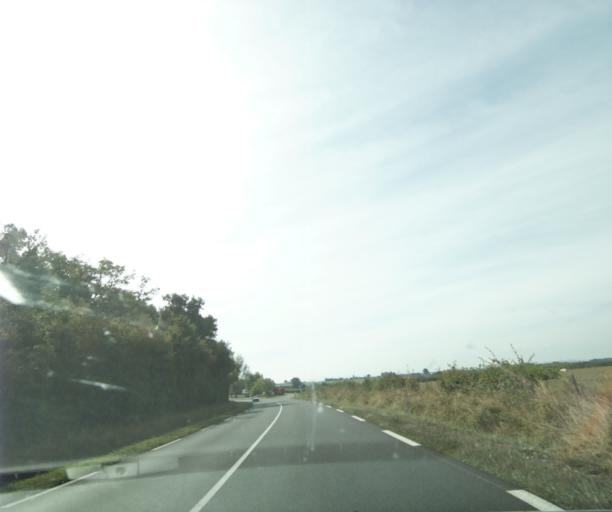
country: FR
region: Auvergne
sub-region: Departement de l'Allier
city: Saint-Francois
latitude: 46.4360
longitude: 3.9073
